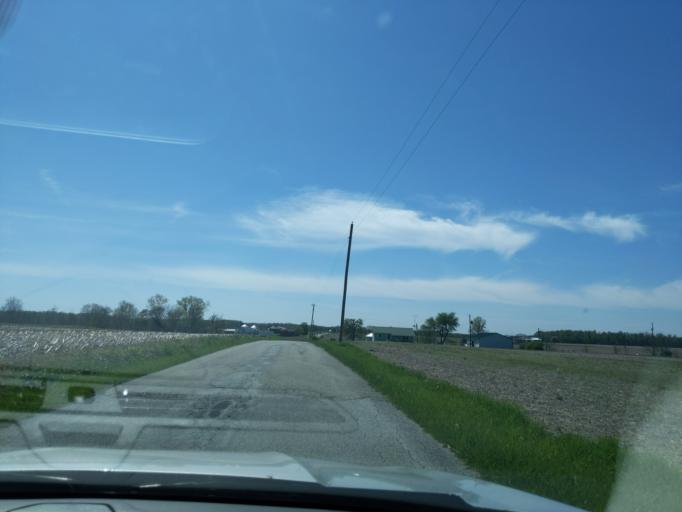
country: US
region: Indiana
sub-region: Decatur County
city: Greensburg
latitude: 39.2481
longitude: -85.4363
